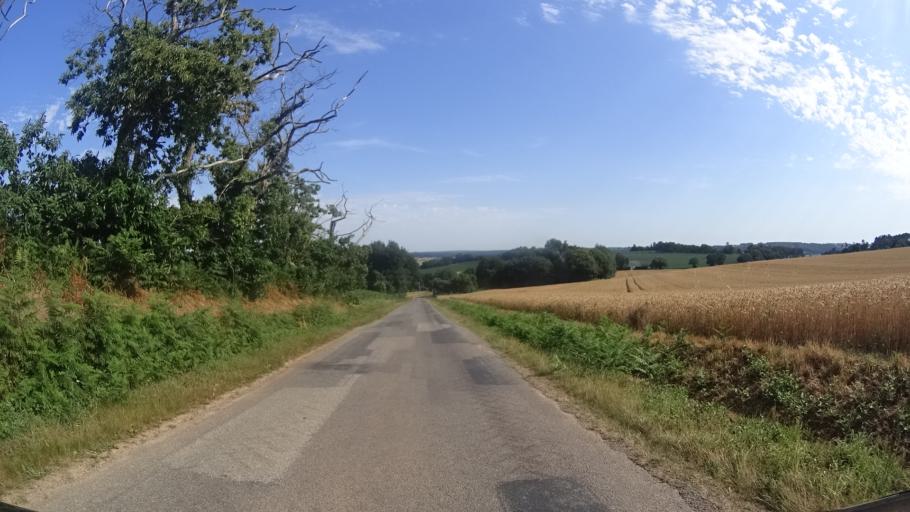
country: FR
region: Brittany
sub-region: Departement du Morbihan
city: Beganne
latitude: 47.6059
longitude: -2.2055
